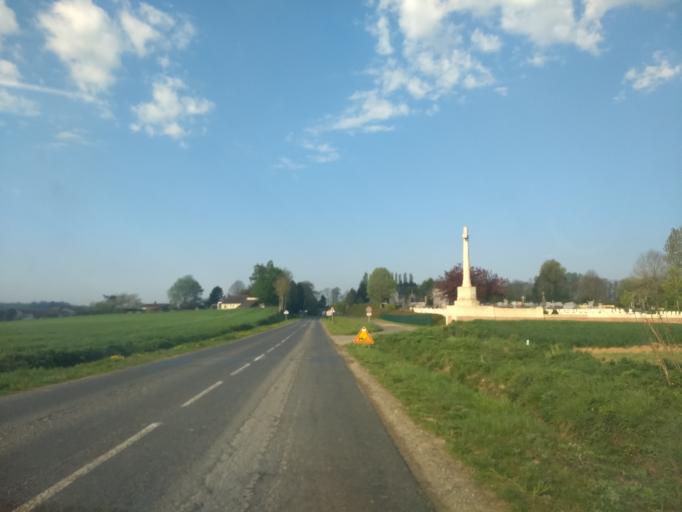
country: FR
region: Picardie
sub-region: Departement de la Somme
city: Corbie
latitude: 50.0131
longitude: 2.5297
